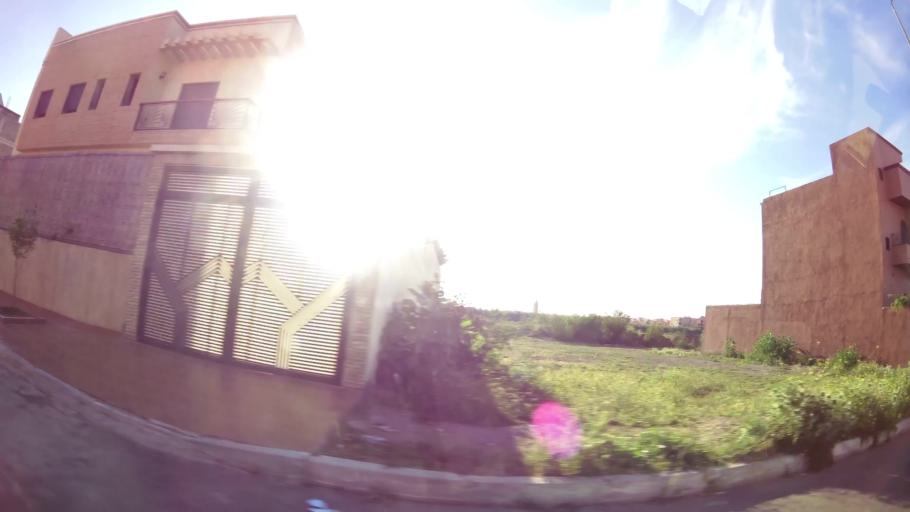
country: MA
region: Marrakech-Tensift-Al Haouz
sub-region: Marrakech
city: Marrakesh
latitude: 31.6808
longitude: -8.0641
